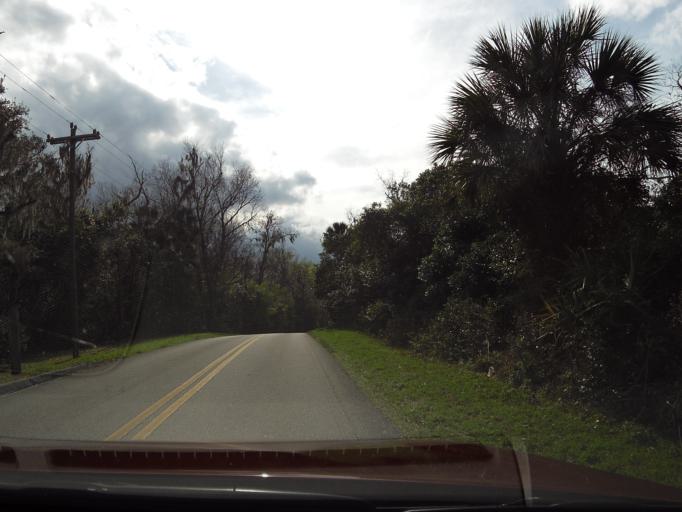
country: US
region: Florida
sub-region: Volusia County
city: De Leon Springs
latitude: 29.1524
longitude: -81.3017
